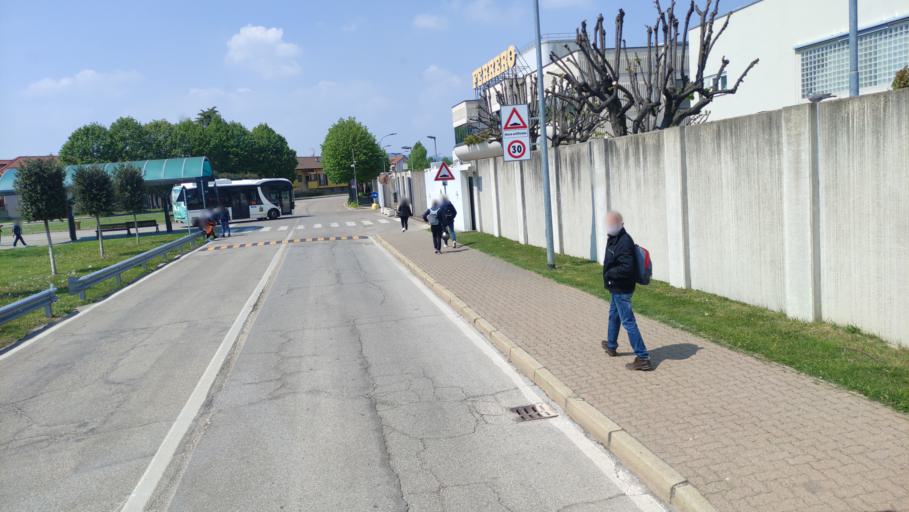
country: IT
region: Piedmont
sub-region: Provincia di Cuneo
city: Alba
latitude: 44.6986
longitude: 8.0236
